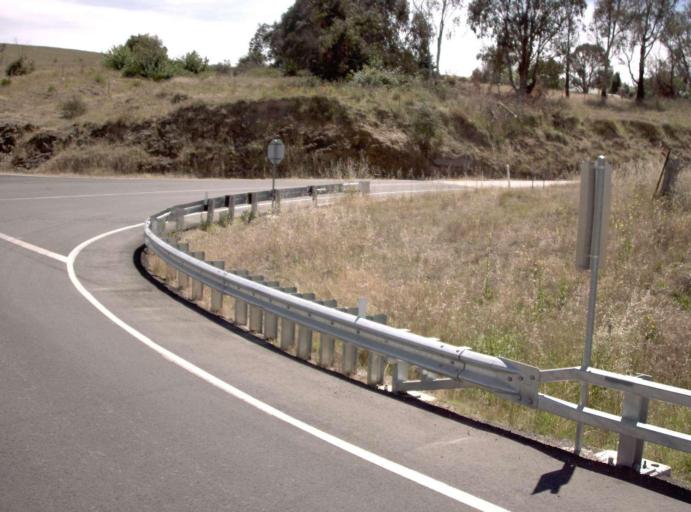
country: AU
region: Victoria
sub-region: Alpine
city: Mount Beauty
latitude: -37.0660
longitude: 147.6032
